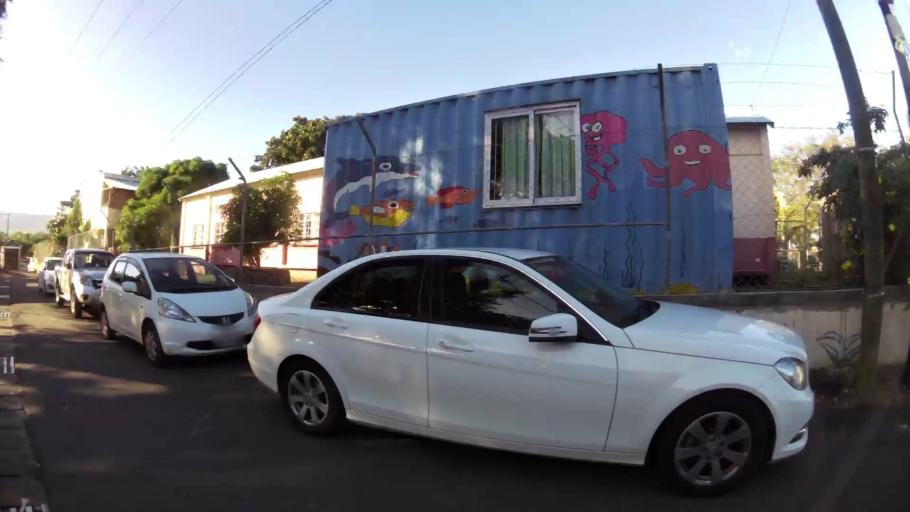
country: MU
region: Black River
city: Tamarin
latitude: -20.3294
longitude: 57.3786
